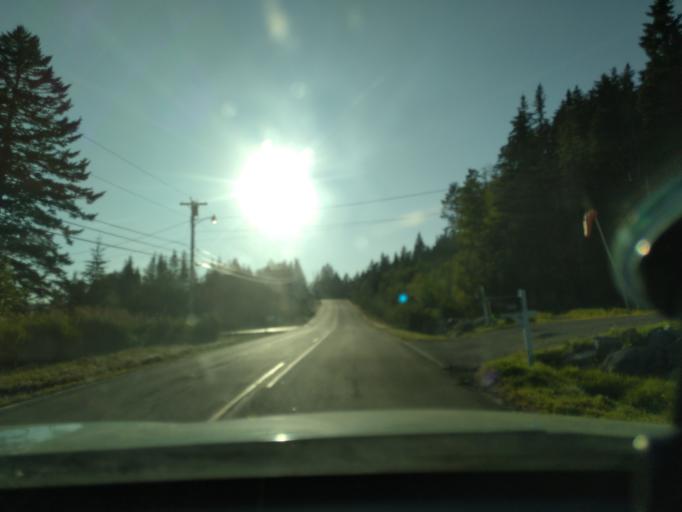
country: US
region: Maine
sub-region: Washington County
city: Machiasport
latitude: 44.6592
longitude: -67.2168
